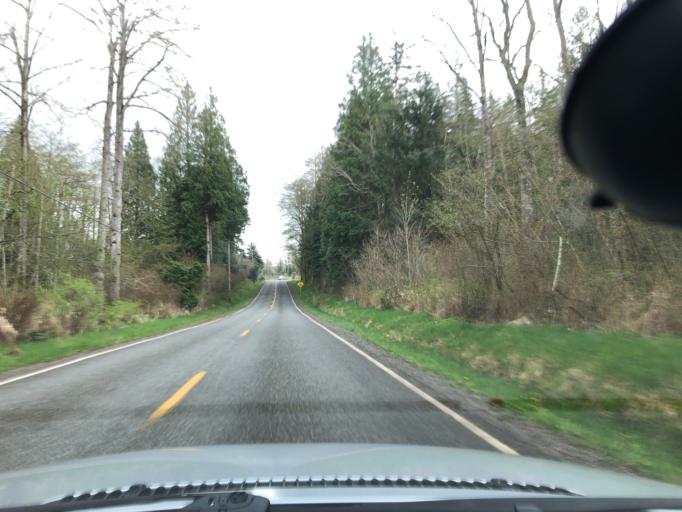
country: US
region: Washington
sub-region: Whatcom County
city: Birch Bay
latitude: 48.8943
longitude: -122.7725
